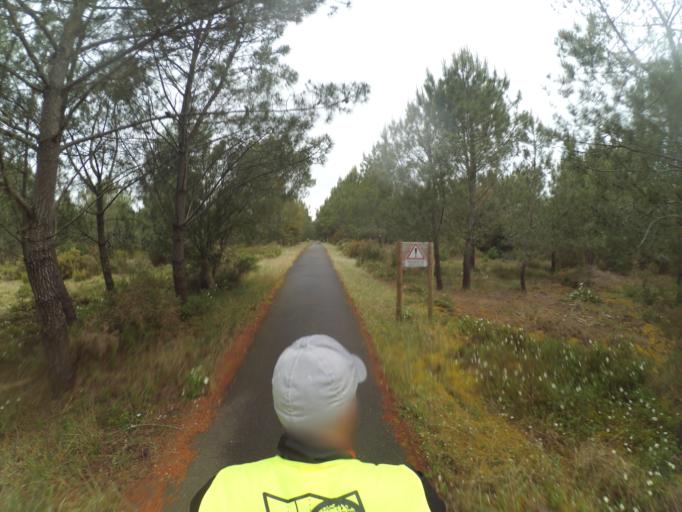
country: FR
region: Aquitaine
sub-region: Departement des Landes
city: Mimizan
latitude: 44.2236
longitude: -1.2585
